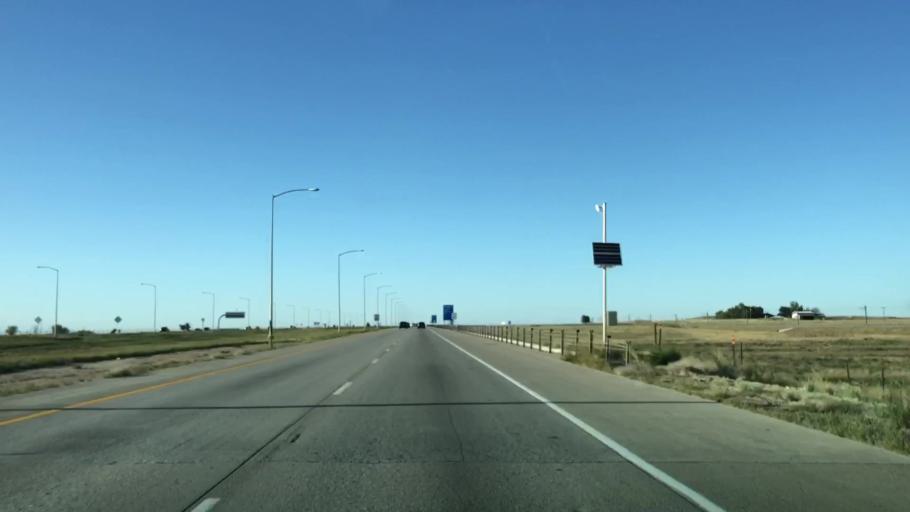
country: US
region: Colorado
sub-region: Adams County
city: Aurora
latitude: 39.8116
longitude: -104.7863
